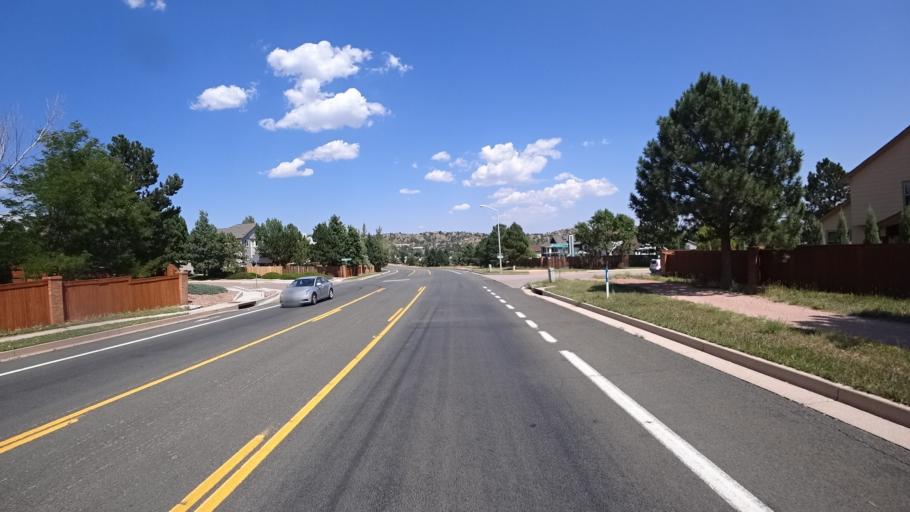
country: US
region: Colorado
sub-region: El Paso County
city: Air Force Academy
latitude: 38.9208
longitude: -104.8684
